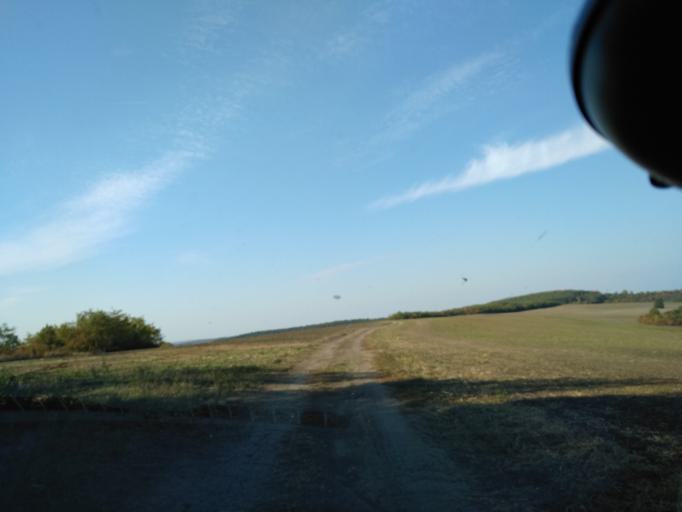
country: RO
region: Timis
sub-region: Comuna Bogda
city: Bogda
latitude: 45.9116
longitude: 21.6033
